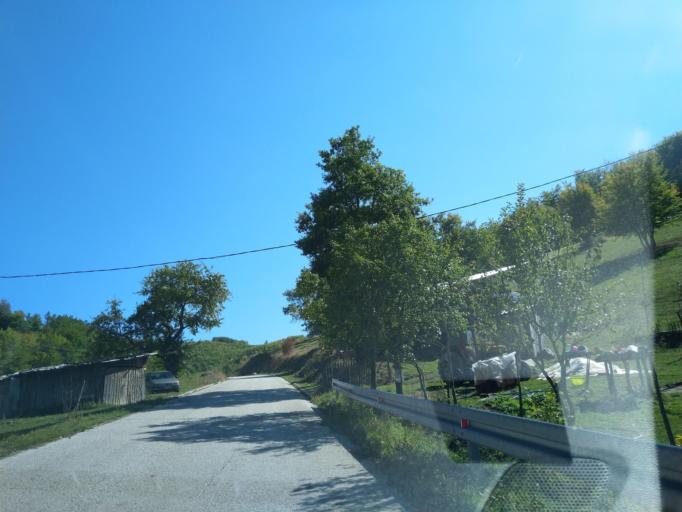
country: RS
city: Sokolovica
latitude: 43.2599
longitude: 20.2995
